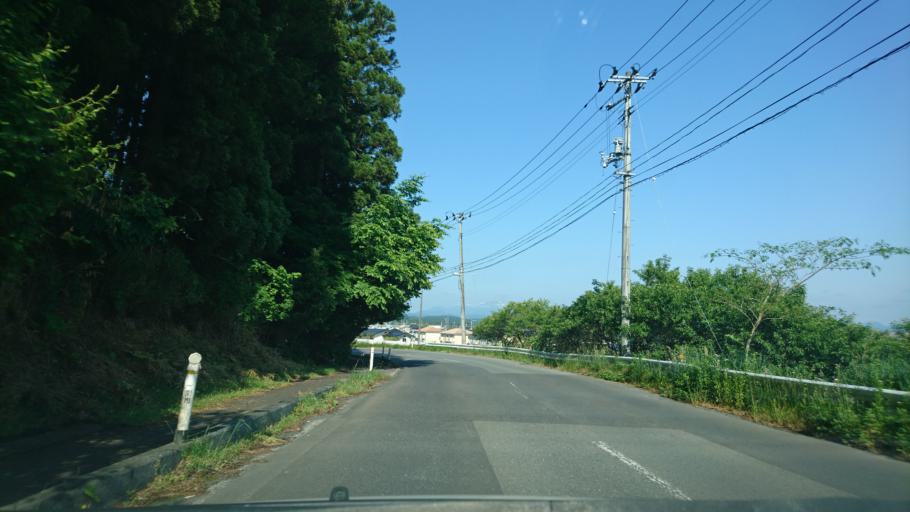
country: JP
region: Iwate
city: Ichinoseki
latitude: 38.9178
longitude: 141.1152
